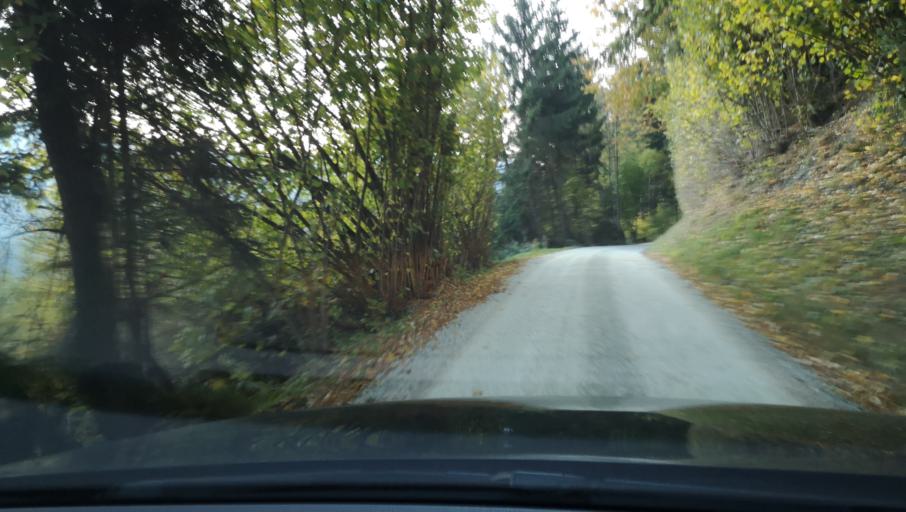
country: AT
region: Styria
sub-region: Politischer Bezirk Weiz
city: Birkfeld
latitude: 47.3562
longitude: 15.6777
